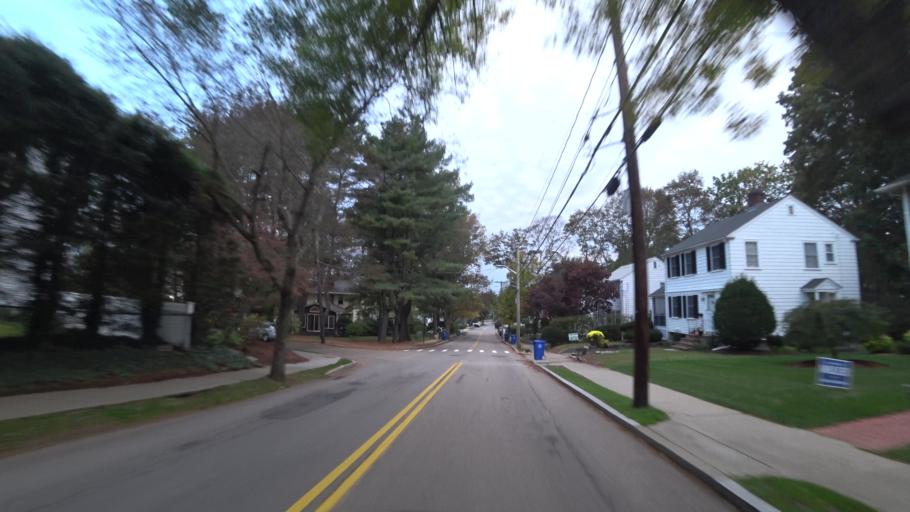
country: US
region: Massachusetts
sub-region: Middlesex County
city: Newton
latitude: 42.3204
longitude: -71.1890
